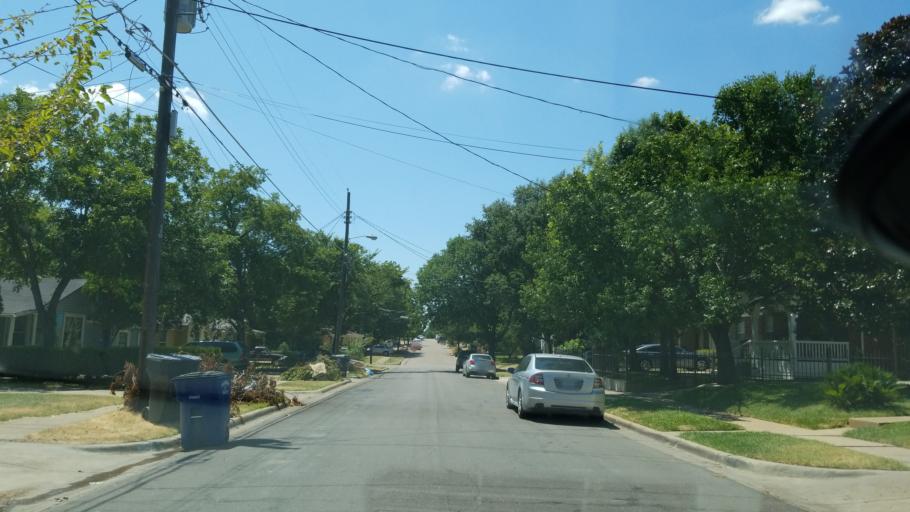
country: US
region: Texas
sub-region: Dallas County
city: Cockrell Hill
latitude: 32.7255
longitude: -96.8843
